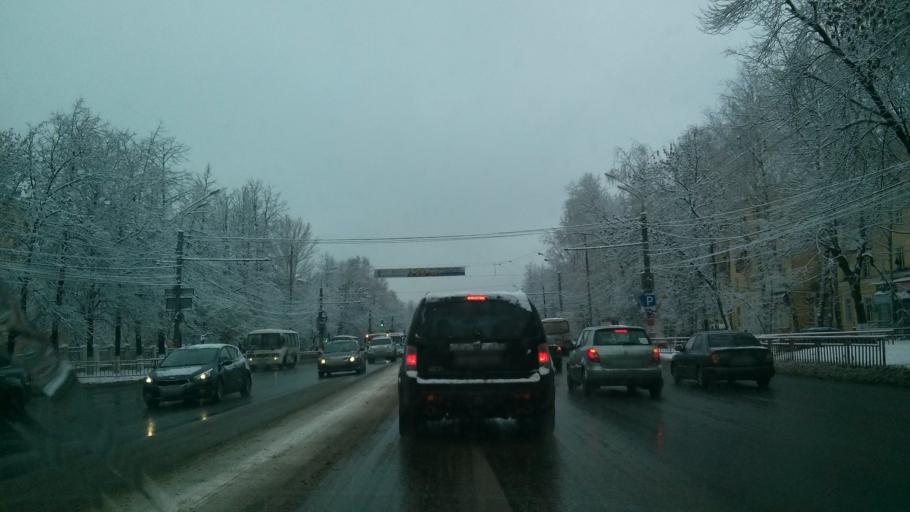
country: RU
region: Nizjnij Novgorod
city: Nizhniy Novgorod
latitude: 56.3030
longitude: 43.9844
